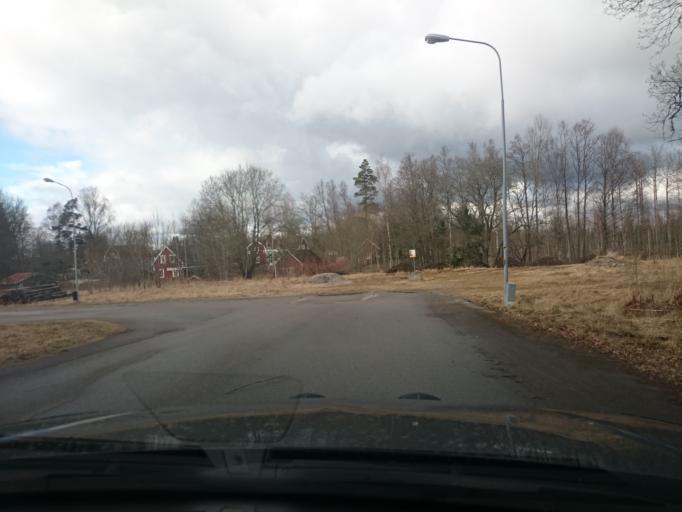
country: SE
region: Joenkoeping
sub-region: Vetlanda Kommun
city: Vetlanda
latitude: 57.3096
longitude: 15.1253
